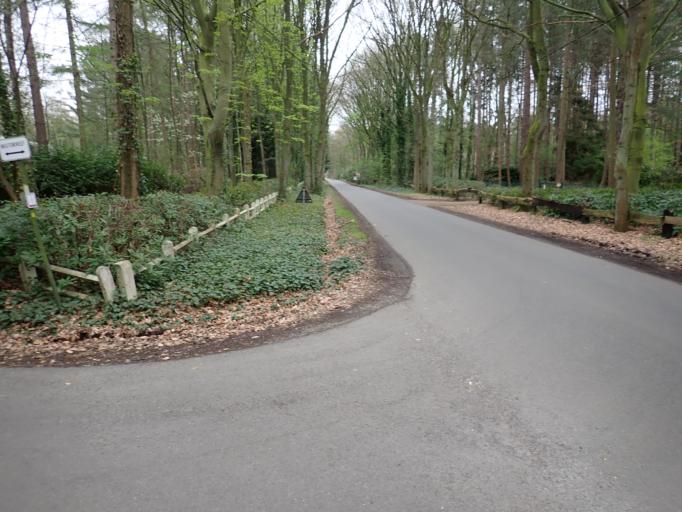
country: BE
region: Flanders
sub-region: Provincie Antwerpen
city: Nijlen
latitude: 51.1896
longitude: 4.6846
